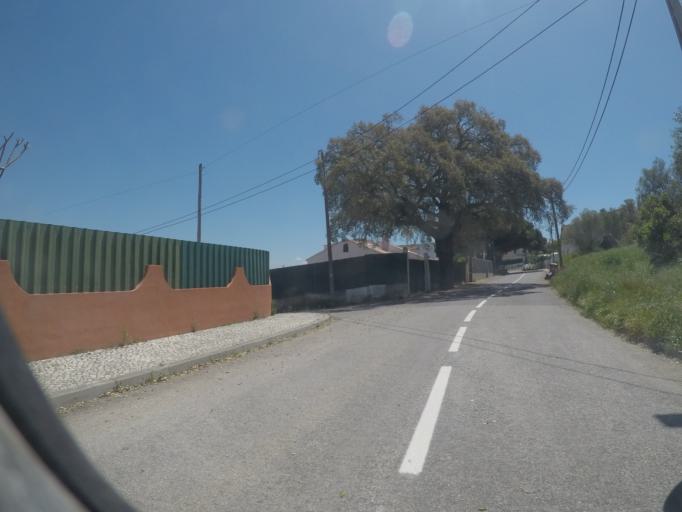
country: PT
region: Setubal
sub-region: Sesimbra
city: Sesimbra
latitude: 38.4614
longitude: -9.0756
